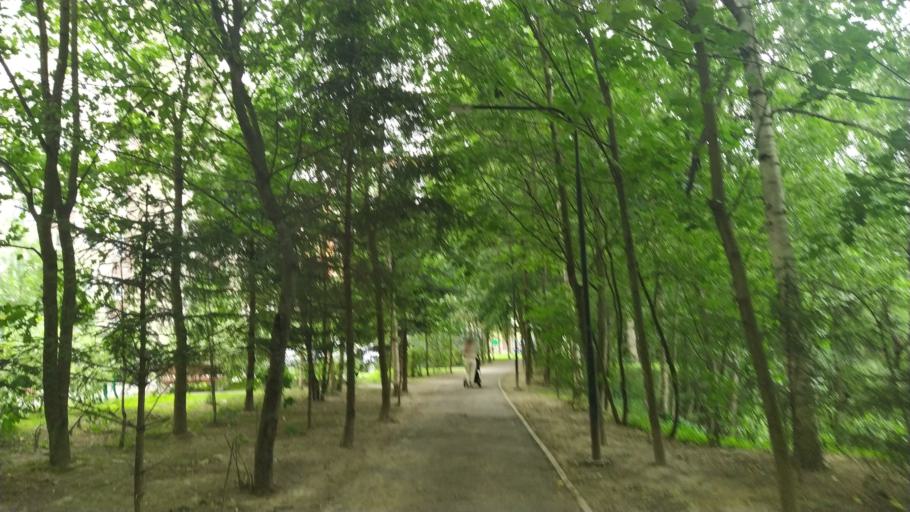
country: RU
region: Leningrad
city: Murino
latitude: 60.0426
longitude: 30.4664
